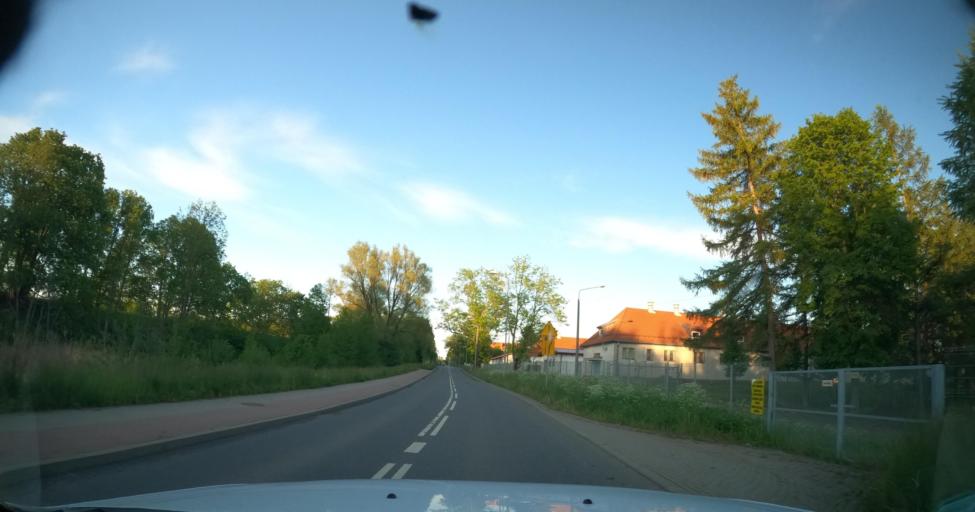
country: PL
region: Warmian-Masurian Voivodeship
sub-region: Powiat lidzbarski
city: Lidzbark Warminski
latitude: 54.1251
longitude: 20.5395
